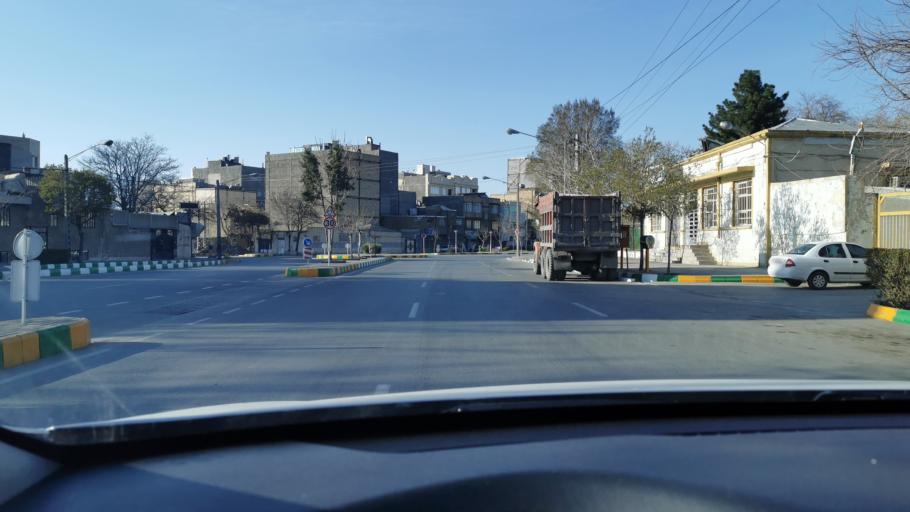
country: IR
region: Razavi Khorasan
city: Mashhad
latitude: 36.3025
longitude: 59.6334
